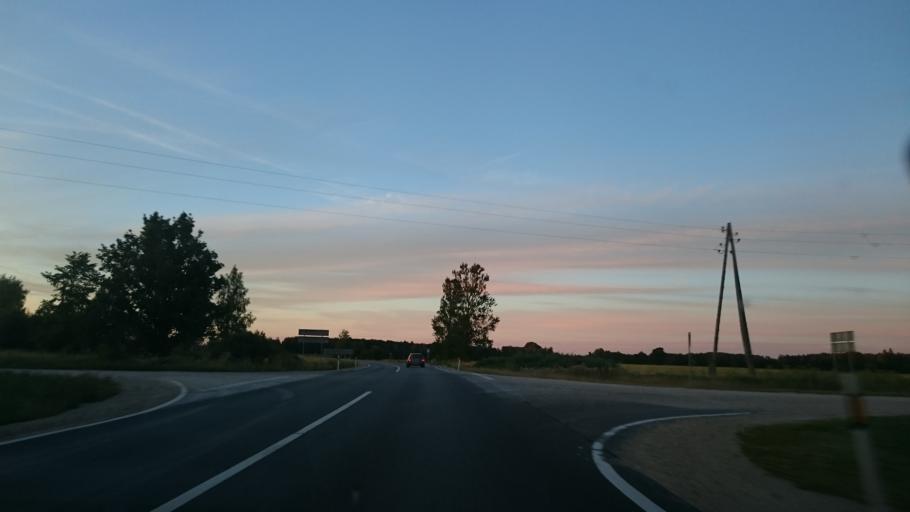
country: LV
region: Dobeles Rajons
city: Dobele
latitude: 56.7079
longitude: 23.1833
